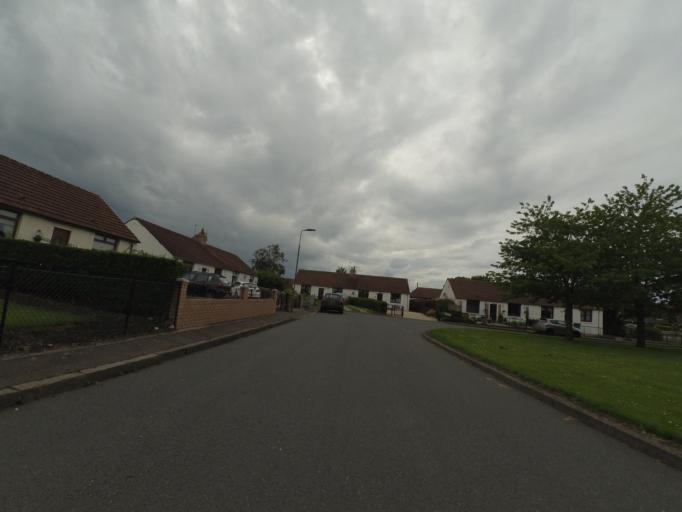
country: GB
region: Scotland
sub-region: East Lothian
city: Macmerry
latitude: 55.9414
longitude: -2.9069
